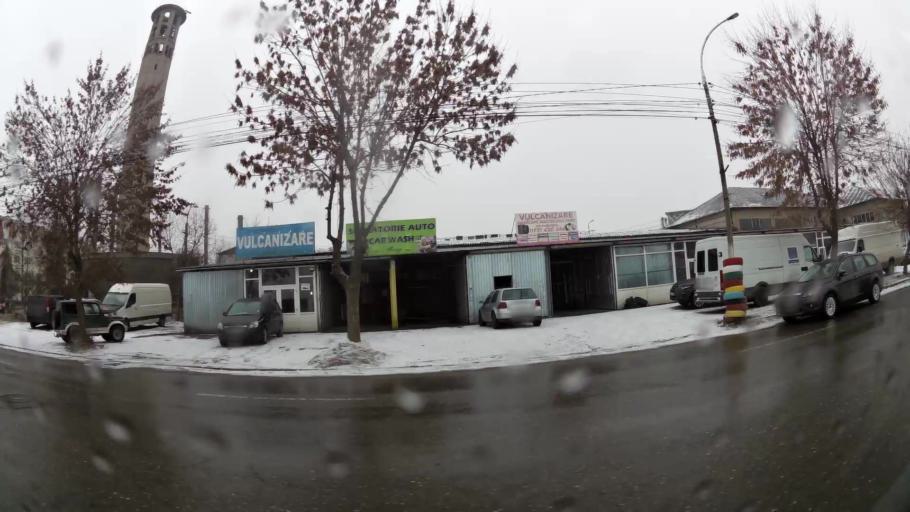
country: RO
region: Dambovita
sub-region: Municipiul Targoviste
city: Targoviste
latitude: 44.9147
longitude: 25.4422
